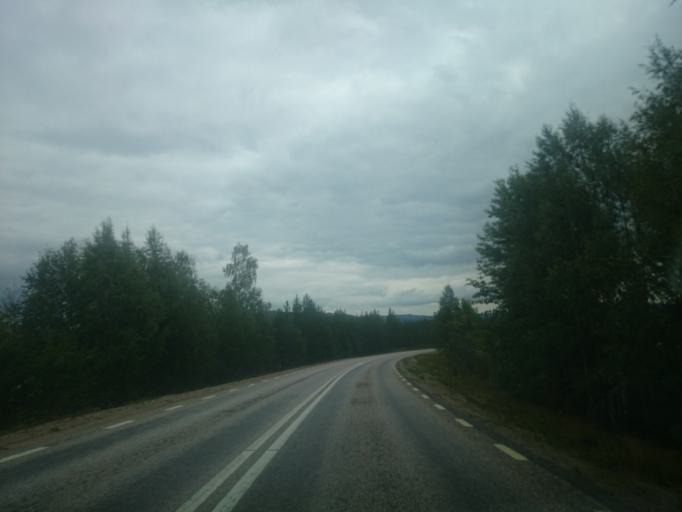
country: SE
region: Gaevleborg
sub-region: Ljusdals Kommun
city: Farila
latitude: 61.9960
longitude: 15.1880
